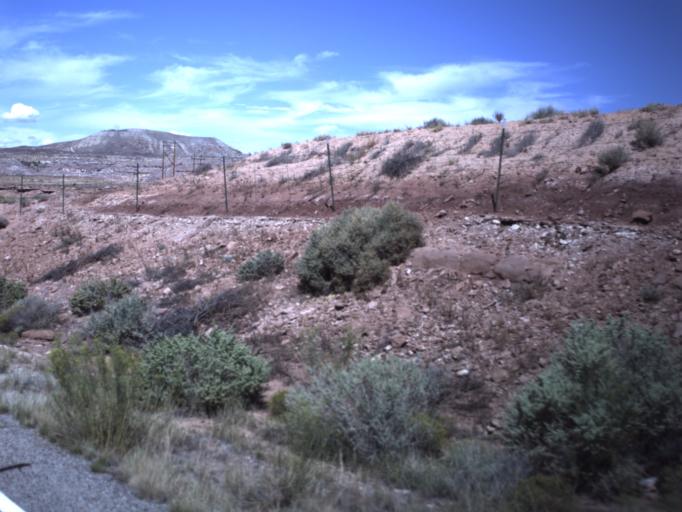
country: US
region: Utah
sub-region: San Juan County
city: Blanding
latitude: 37.2894
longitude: -109.3983
